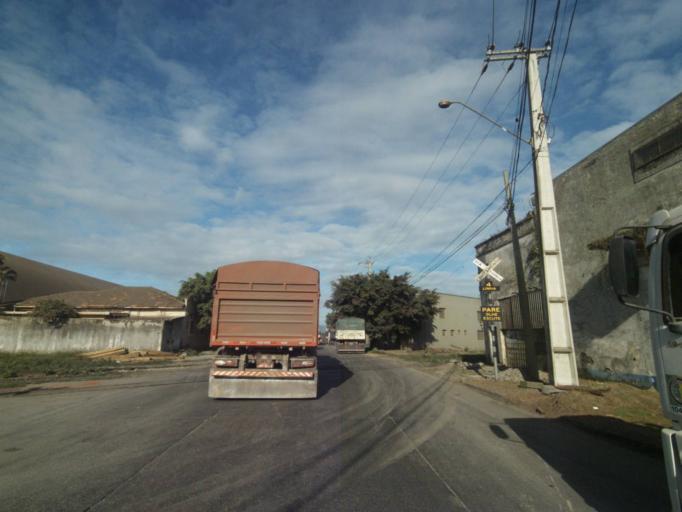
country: BR
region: Parana
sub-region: Paranagua
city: Paranagua
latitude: -25.5073
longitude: -48.5188
